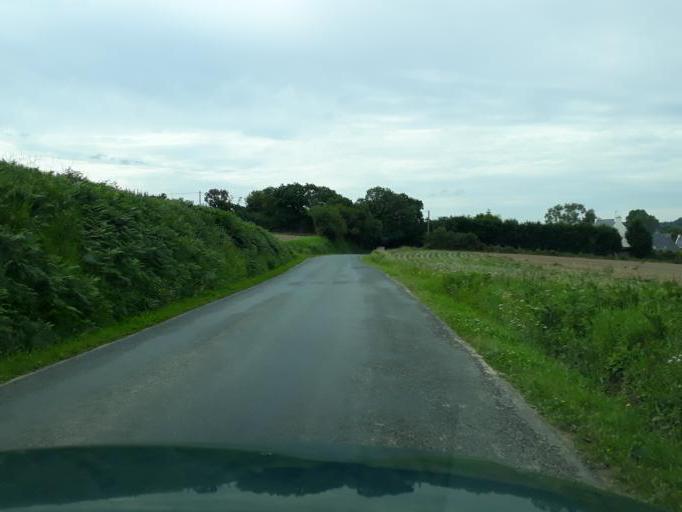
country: FR
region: Brittany
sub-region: Departement des Cotes-d'Armor
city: Paimpol
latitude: 48.7678
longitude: -3.0442
